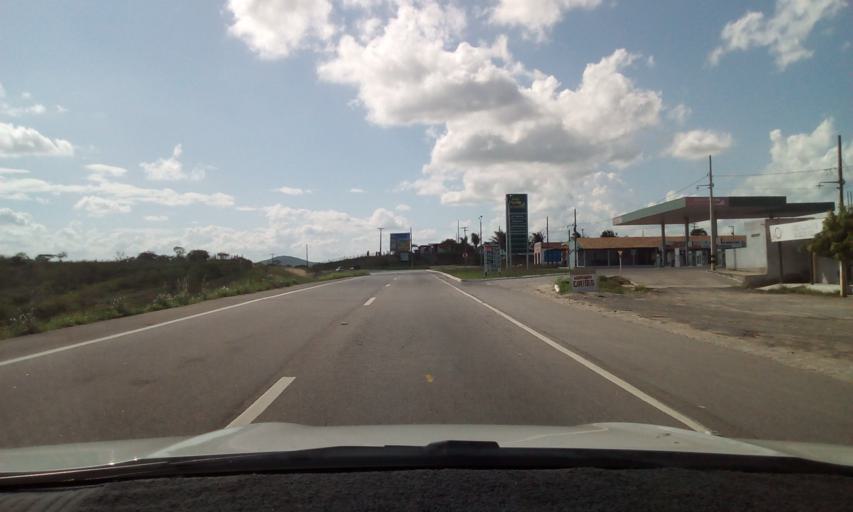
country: BR
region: Paraiba
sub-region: Gurinhem
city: Gurinhem
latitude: -7.1681
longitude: -35.3336
